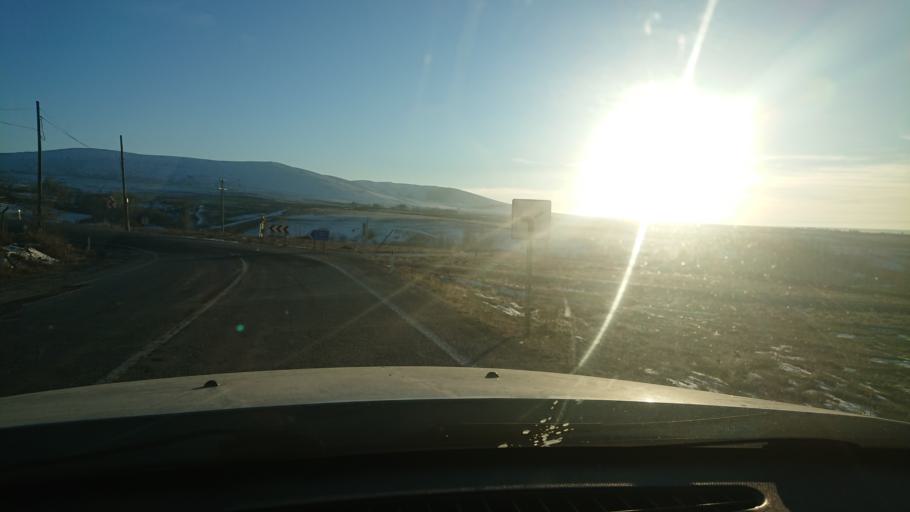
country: TR
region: Aksaray
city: Ortakoy
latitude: 38.7550
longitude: 33.9329
